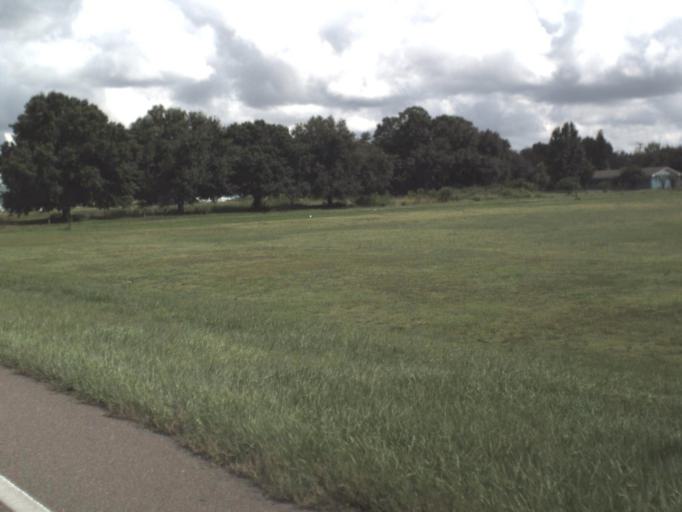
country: US
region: Florida
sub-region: Hardee County
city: Zolfo Springs
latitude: 27.5002
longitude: -81.8064
